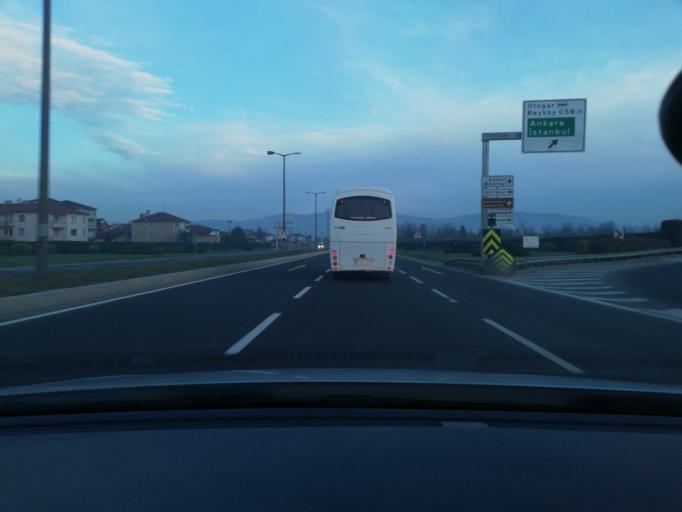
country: TR
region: Duzce
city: Duzce
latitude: 40.8379
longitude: 31.1738
